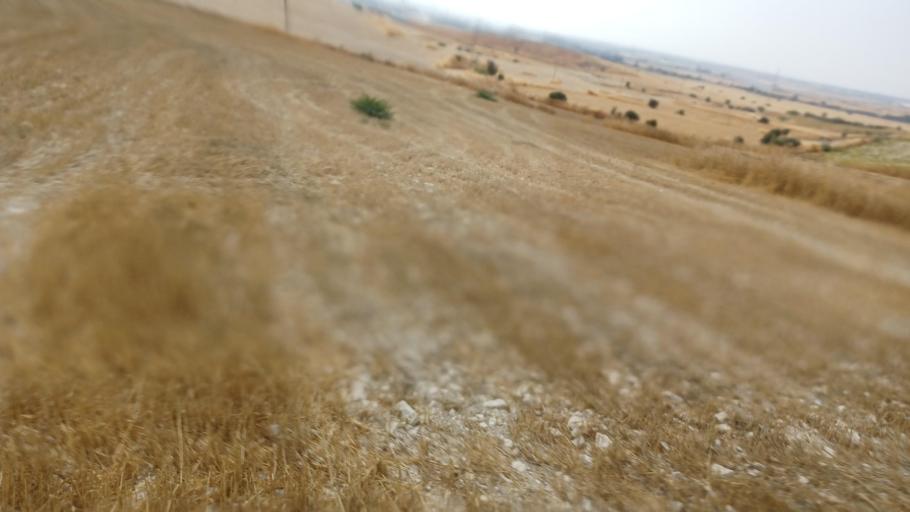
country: CY
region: Larnaka
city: Dhromolaxia
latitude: 34.9134
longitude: 33.5459
